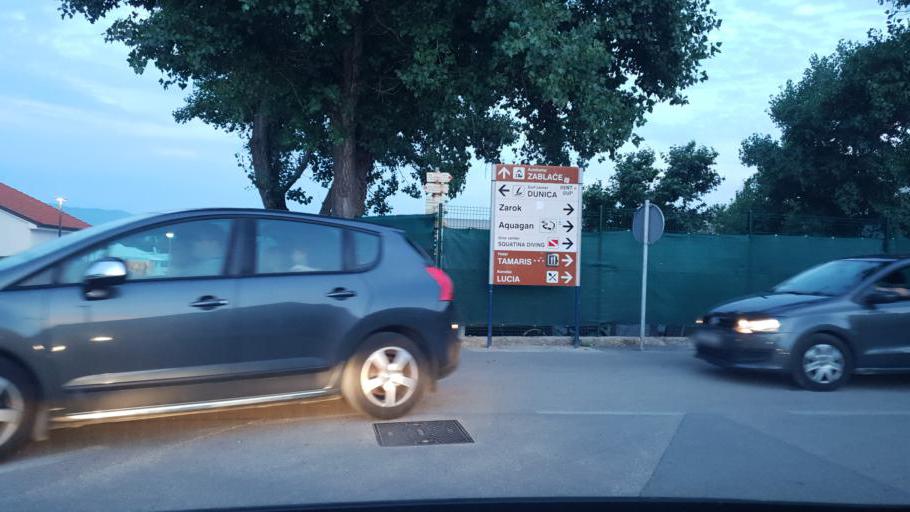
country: HR
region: Primorsko-Goranska
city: Punat
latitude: 44.9656
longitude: 14.7477
